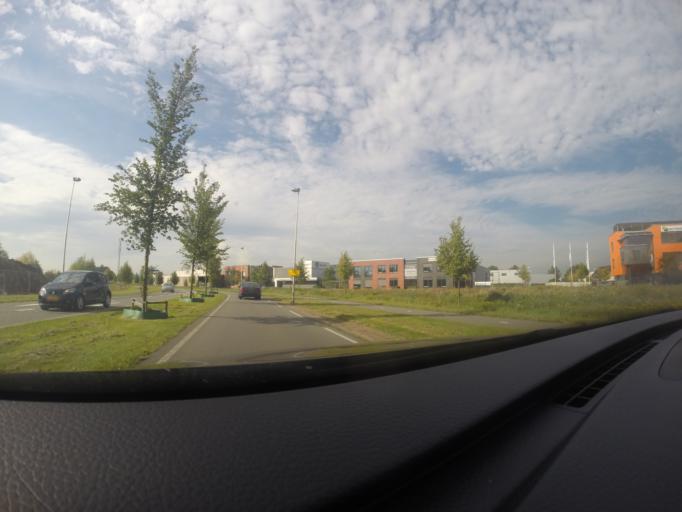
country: NL
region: Gelderland
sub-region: Gemeente Doetinchem
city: Doetinchem
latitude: 51.9533
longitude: 6.2984
